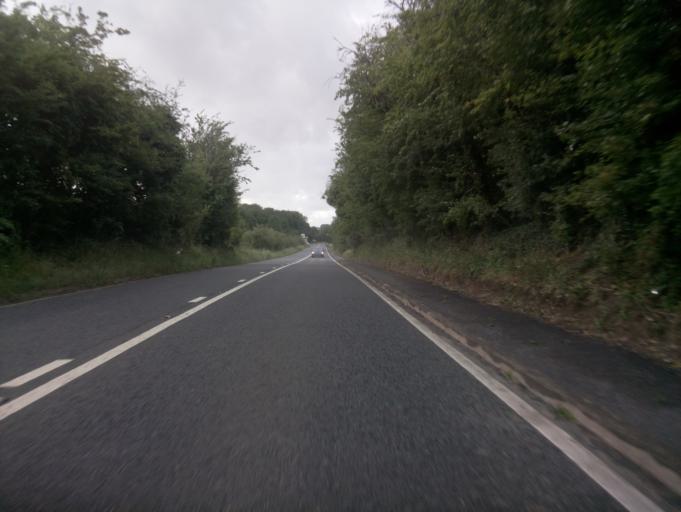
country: GB
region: England
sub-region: Gloucestershire
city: Shipton Village
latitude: 51.8676
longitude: -1.9613
